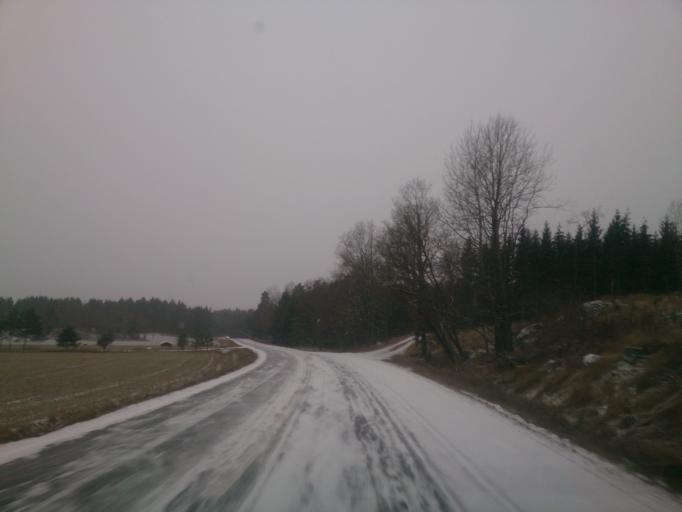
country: SE
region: OEstergoetland
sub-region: Norrkopings Kommun
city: Norrkoping
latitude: 58.4915
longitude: 16.1491
